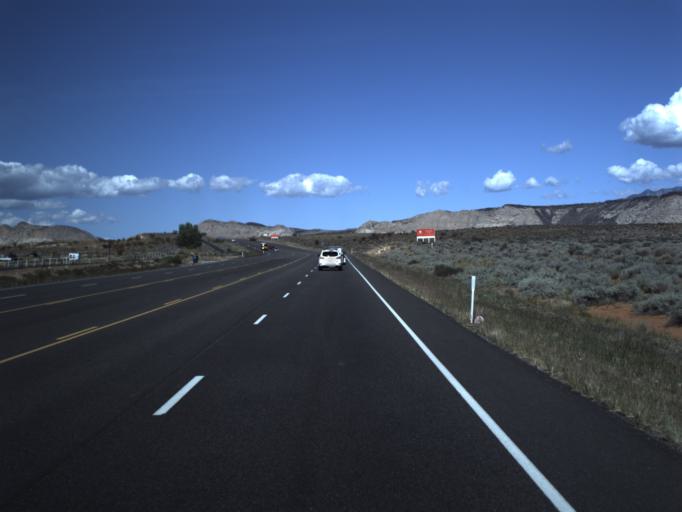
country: US
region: Utah
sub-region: Washington County
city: Santa Clara
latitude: 37.1836
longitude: -113.6192
